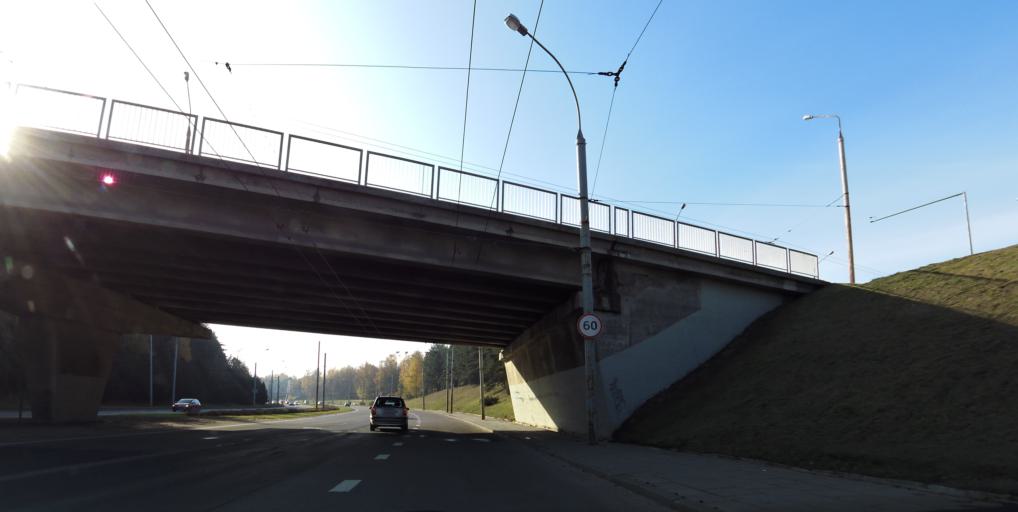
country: LT
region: Vilnius County
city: Lazdynai
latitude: 54.6881
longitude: 25.2094
